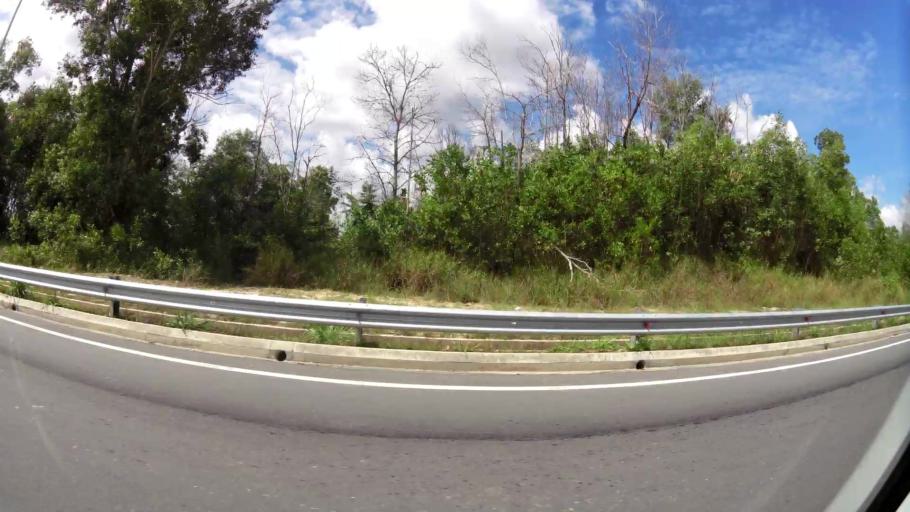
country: BN
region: Brunei and Muara
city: Bandar Seri Begawan
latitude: 4.9323
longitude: 114.8883
